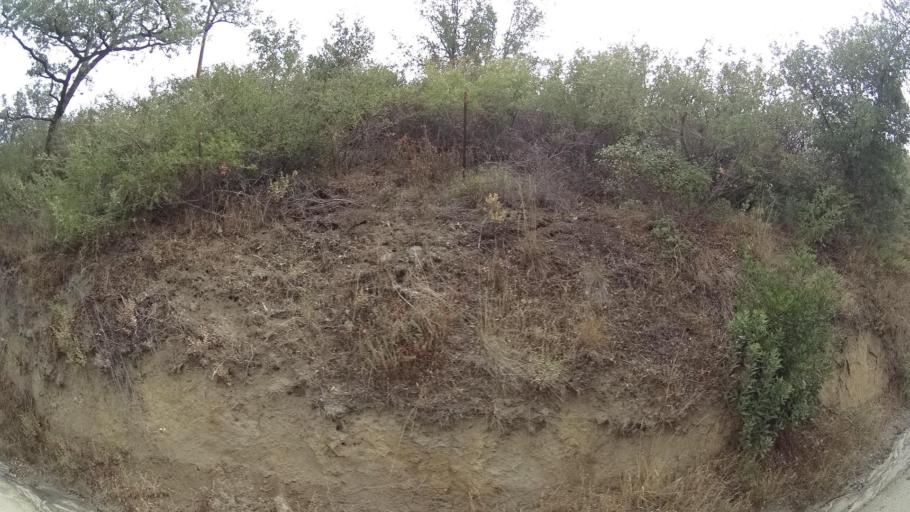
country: US
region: California
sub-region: San Diego County
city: Descanso
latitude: 32.9562
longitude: -116.6454
